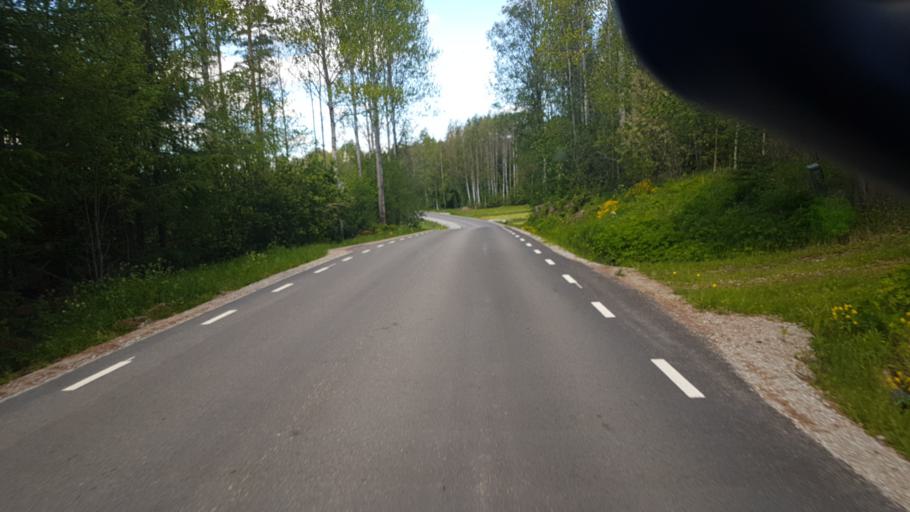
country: SE
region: Vaermland
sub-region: Arvika Kommun
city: Arvika
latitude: 59.6532
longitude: 12.8075
